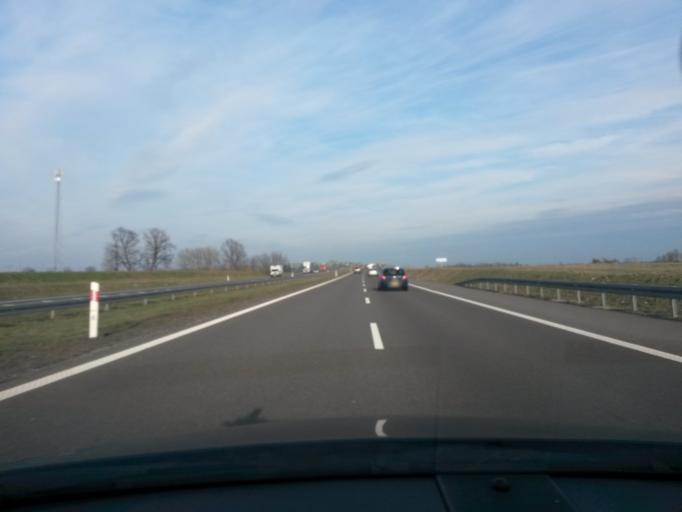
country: PL
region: Lodz Voivodeship
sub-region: Powiat zgierski
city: Strykow
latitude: 51.8982
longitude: 19.5063
